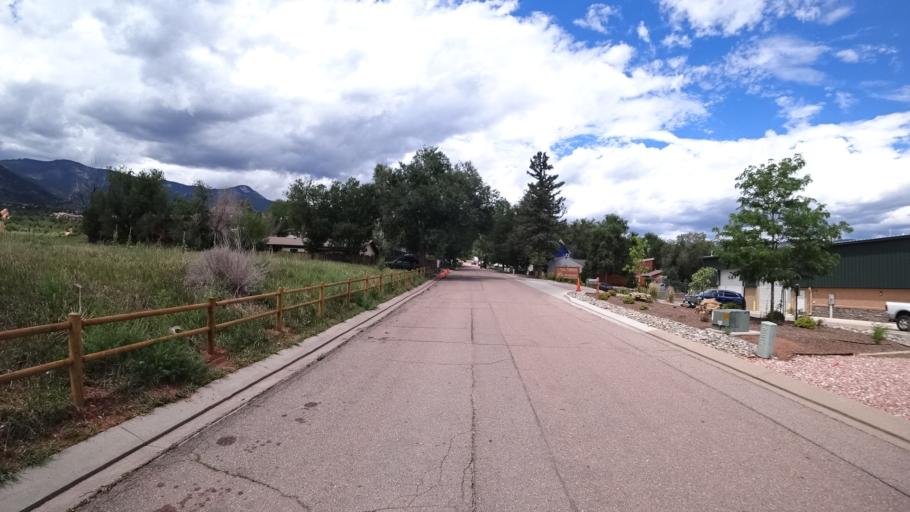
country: US
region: Colorado
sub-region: El Paso County
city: Manitou Springs
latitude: 38.8539
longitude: -104.8841
